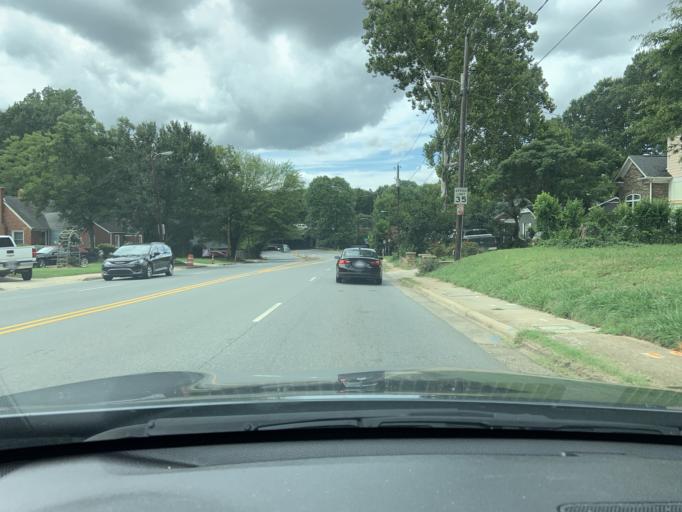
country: US
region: North Carolina
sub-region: Mecklenburg County
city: Charlotte
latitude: 35.2172
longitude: -80.8700
